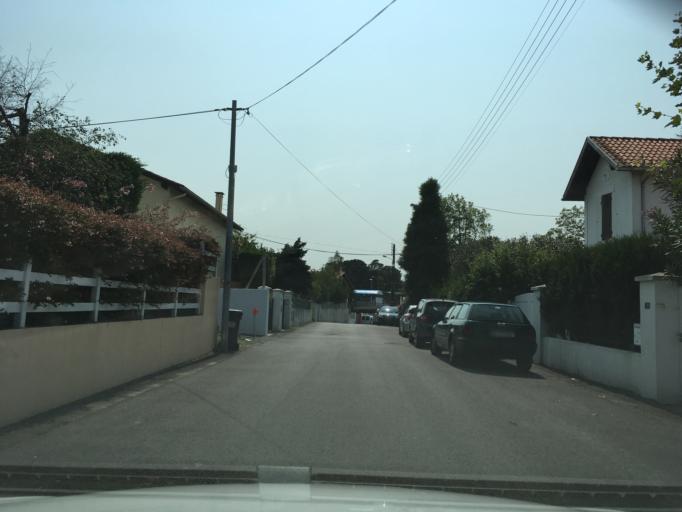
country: FR
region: Aquitaine
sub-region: Departement des Pyrenees-Atlantiques
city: Anglet
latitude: 43.4939
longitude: -1.5319
